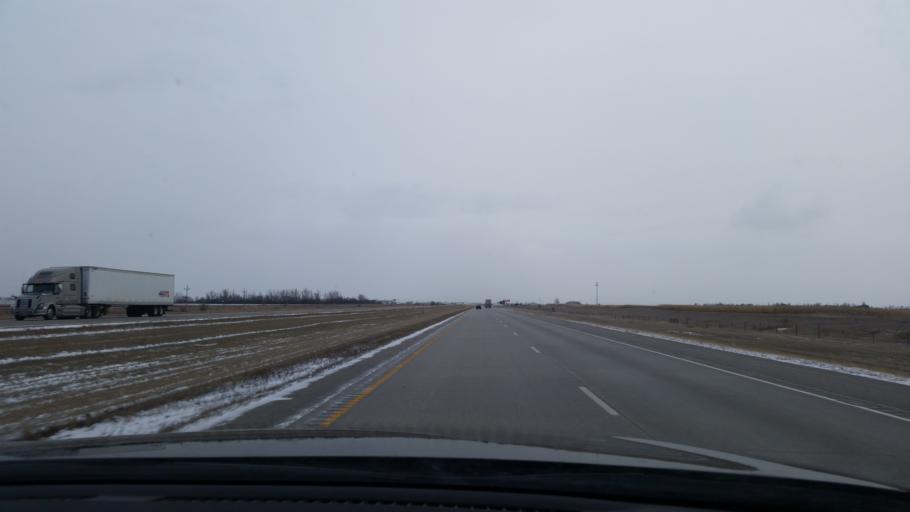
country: US
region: North Dakota
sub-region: Cass County
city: West Fargo
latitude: 46.9583
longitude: -96.8663
